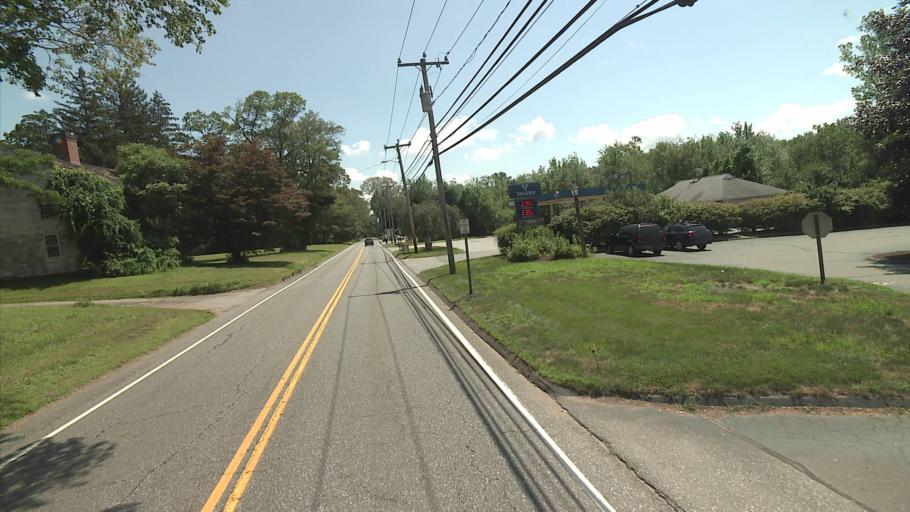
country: US
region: Connecticut
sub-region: Middlesex County
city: Chester Center
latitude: 41.4200
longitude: -72.4448
